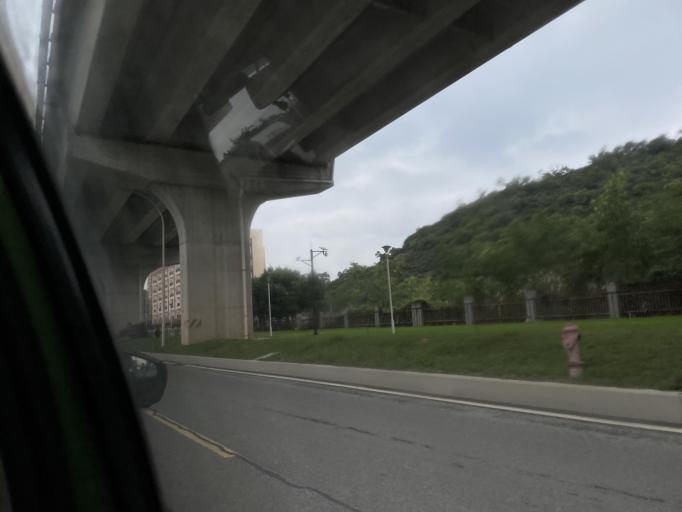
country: CN
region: Guangdong
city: Nanping
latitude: 22.1765
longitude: 113.4802
